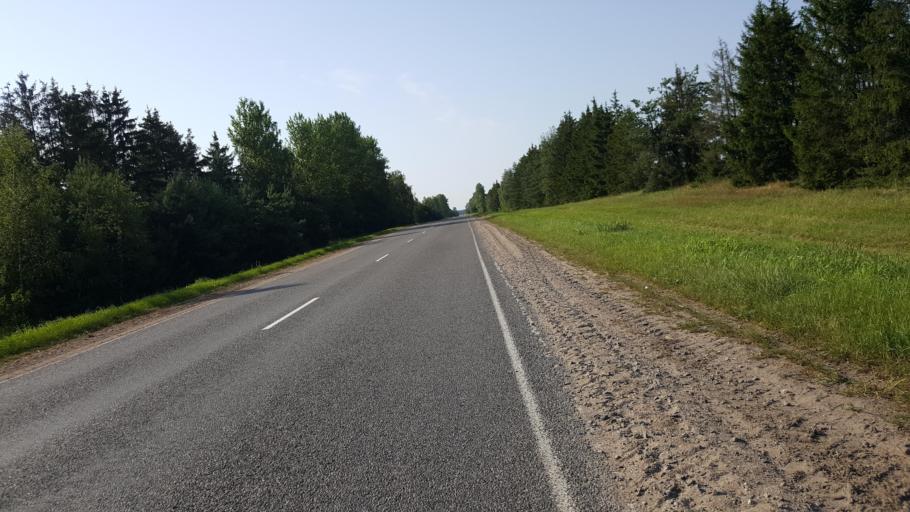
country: BY
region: Brest
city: Kamyanyets
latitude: 52.3498
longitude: 23.9005
